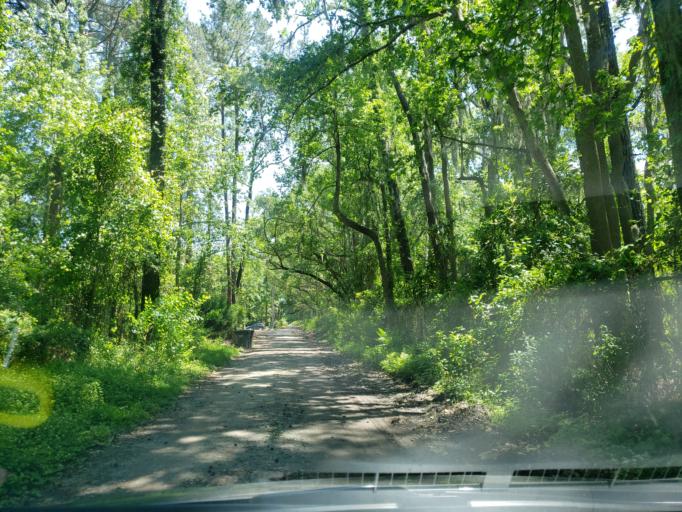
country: US
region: Georgia
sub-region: Chatham County
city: Whitemarsh Island
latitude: 32.0538
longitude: -81.0198
